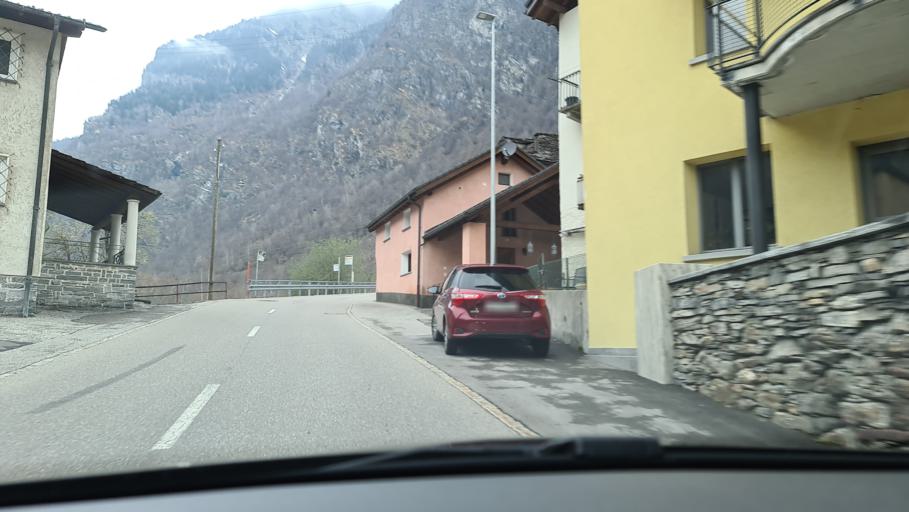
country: CH
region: Ticino
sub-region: Vallemaggia District
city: Cevio
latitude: 46.4064
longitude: 8.6480
